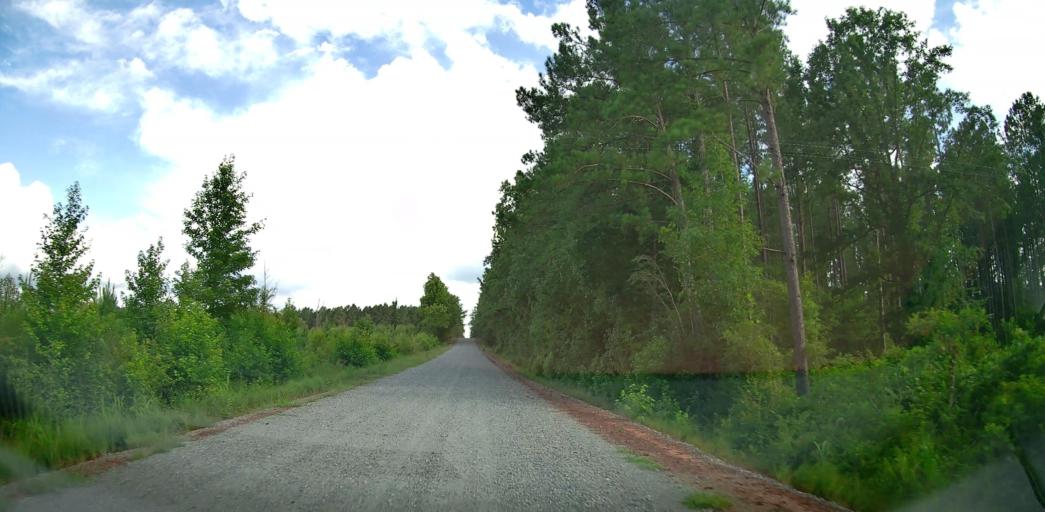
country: US
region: Georgia
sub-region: Bleckley County
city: Cochran
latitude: 32.4254
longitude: -83.4542
